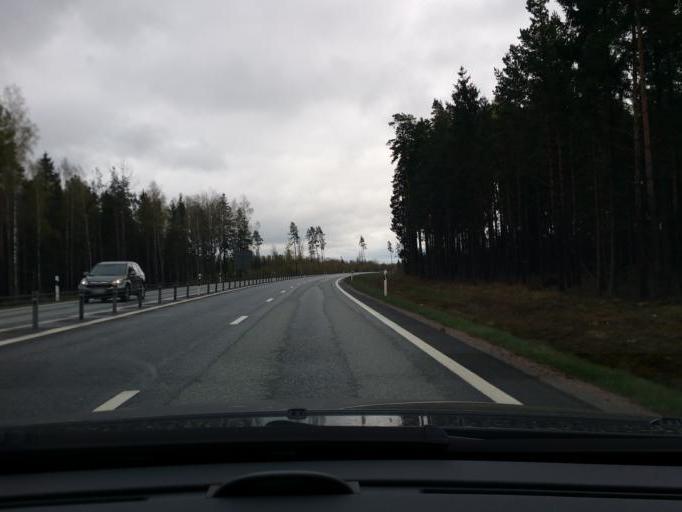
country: SE
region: Kronoberg
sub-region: Vaxjo Kommun
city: Vaexjoe
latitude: 56.9077
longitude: 14.7258
